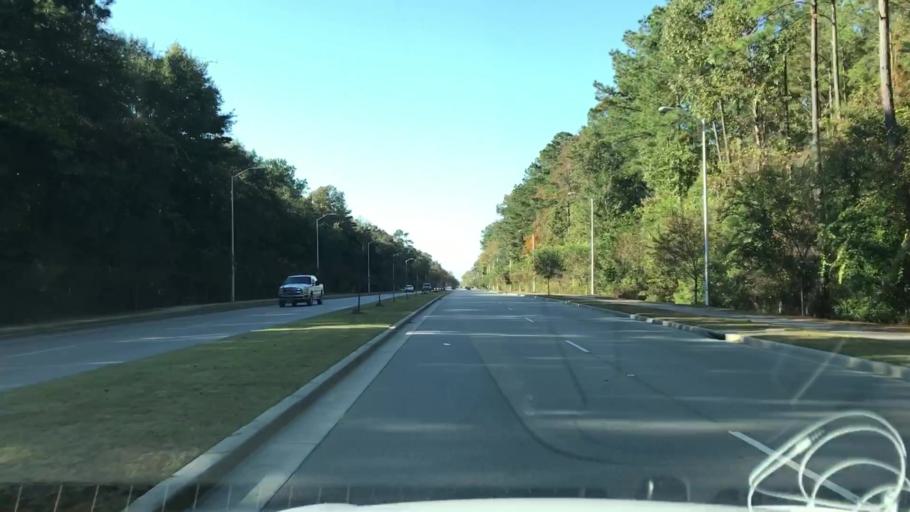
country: US
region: South Carolina
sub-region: Charleston County
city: Shell Point
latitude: 32.8167
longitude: -80.0977
